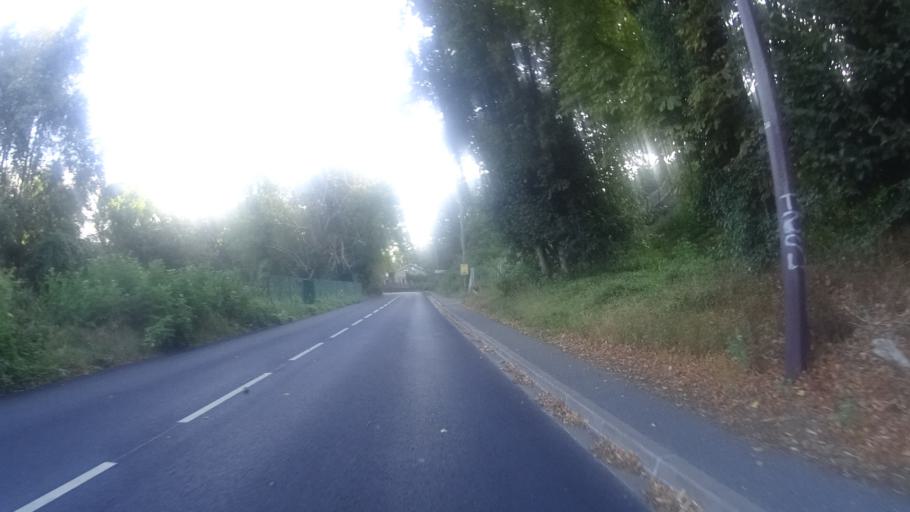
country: FR
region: Ile-de-France
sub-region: Departement de l'Essonne
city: Ormoy
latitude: 48.5787
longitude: 2.4703
